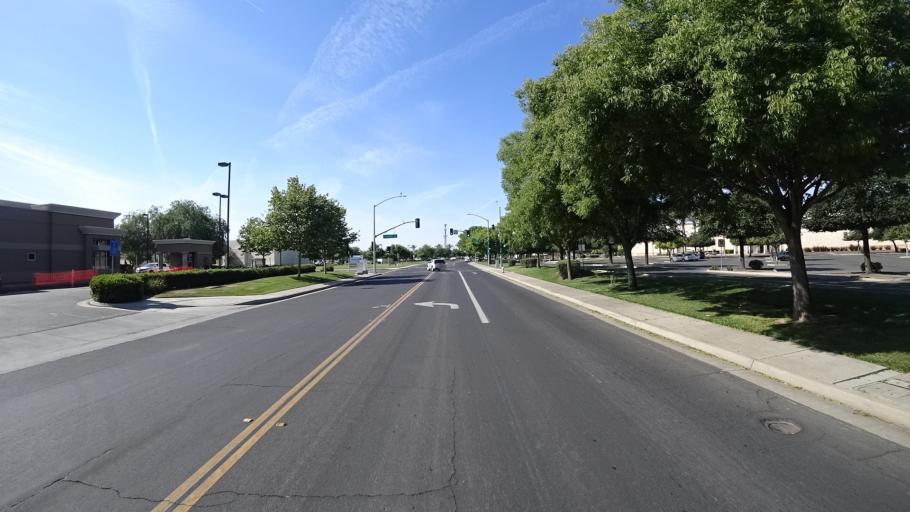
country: US
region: California
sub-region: Kings County
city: Hanford
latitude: 36.3261
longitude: -119.6685
